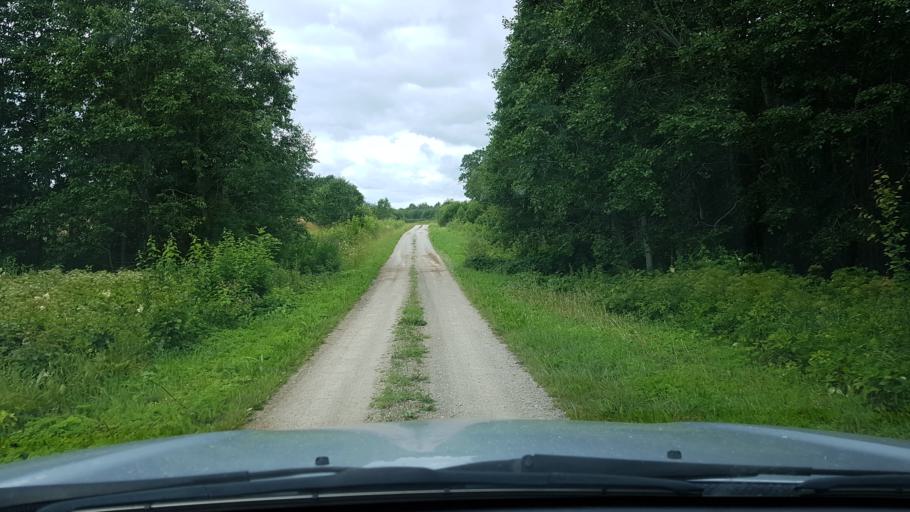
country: EE
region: Ida-Virumaa
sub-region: Narva-Joesuu linn
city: Narva-Joesuu
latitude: 59.4047
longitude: 27.9687
